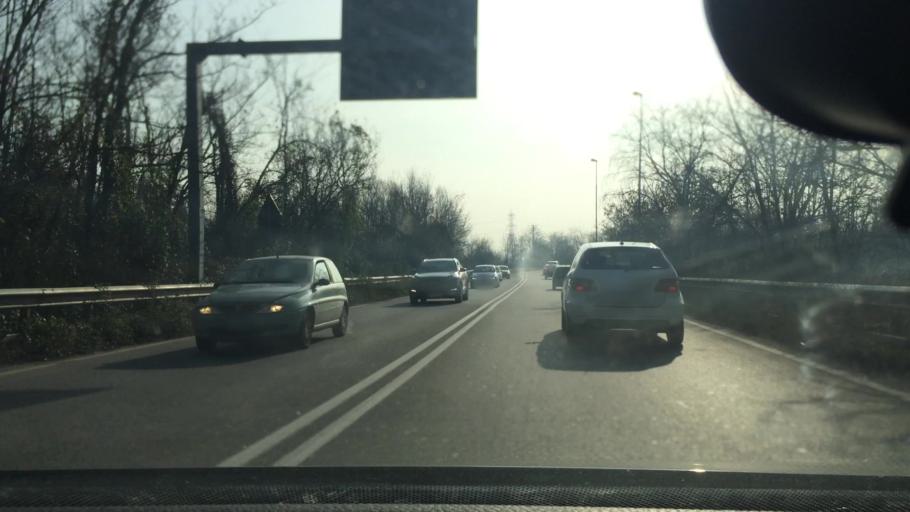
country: IT
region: Lombardy
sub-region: Citta metropolitana di Milano
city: Garbagnate Milanese
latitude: 45.5740
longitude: 9.0943
